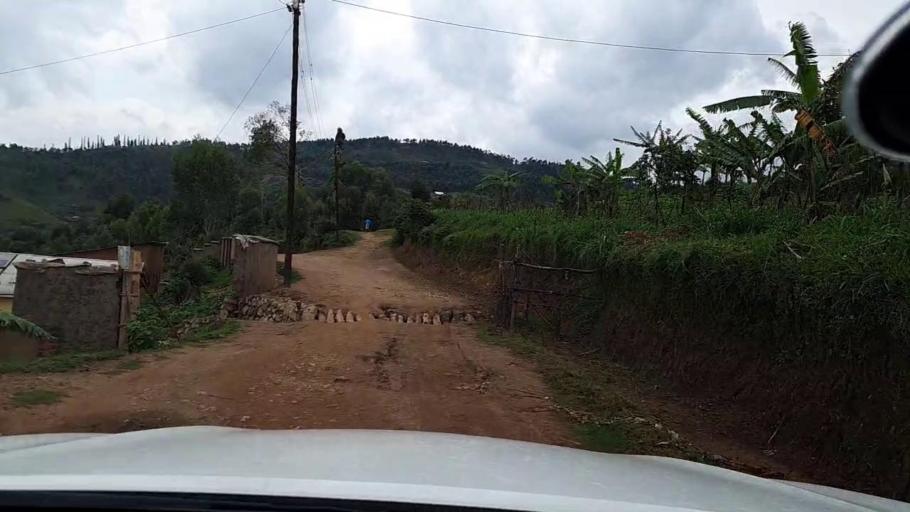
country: RW
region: Western Province
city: Kibuye
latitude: -2.1871
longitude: 29.2943
